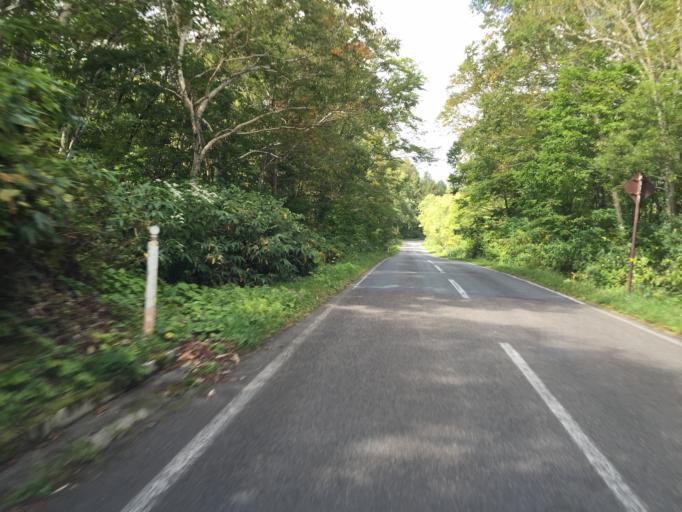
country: JP
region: Fukushima
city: Inawashiro
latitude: 37.6273
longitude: 140.0516
